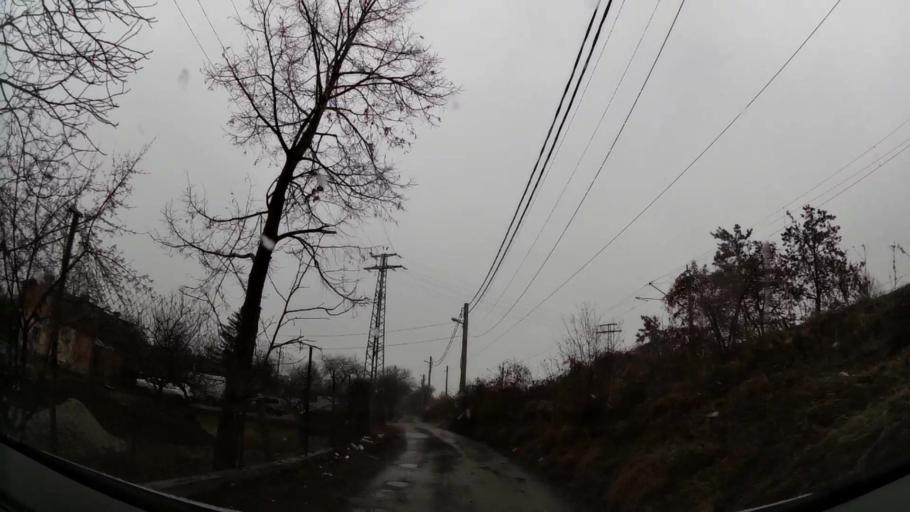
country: BG
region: Sofia-Capital
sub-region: Stolichna Obshtina
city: Sofia
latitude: 42.6618
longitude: 23.4263
